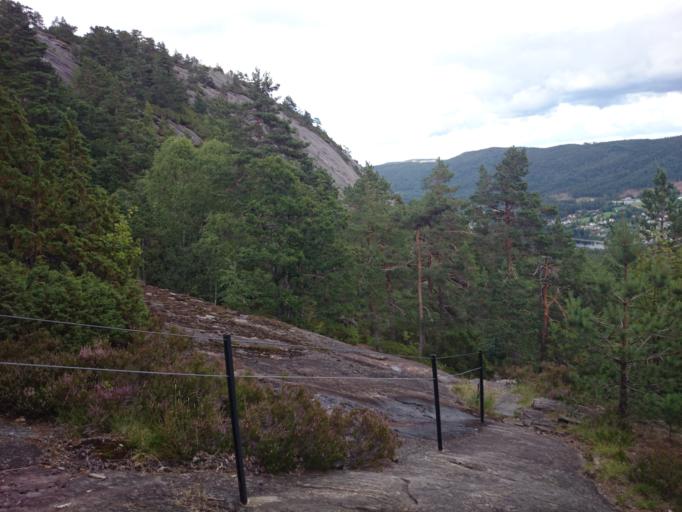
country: NO
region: Aust-Agder
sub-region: Amli
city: Amli
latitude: 58.7689
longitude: 8.4642
